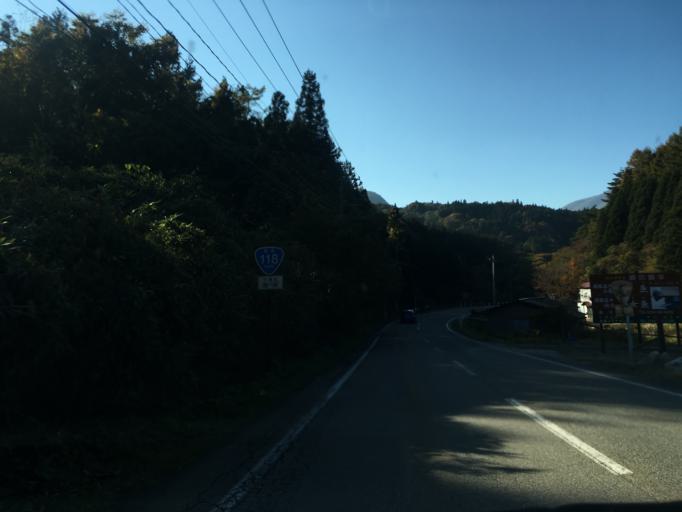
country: JP
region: Fukushima
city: Inawashiro
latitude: 37.2994
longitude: 139.9485
